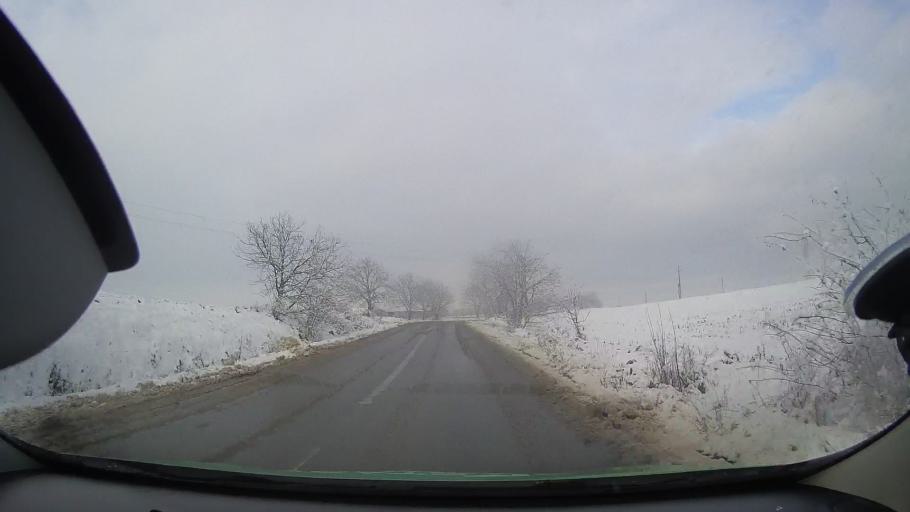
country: RO
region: Mures
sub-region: Comuna Atintis
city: Atintis
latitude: 46.4388
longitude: 24.0930
